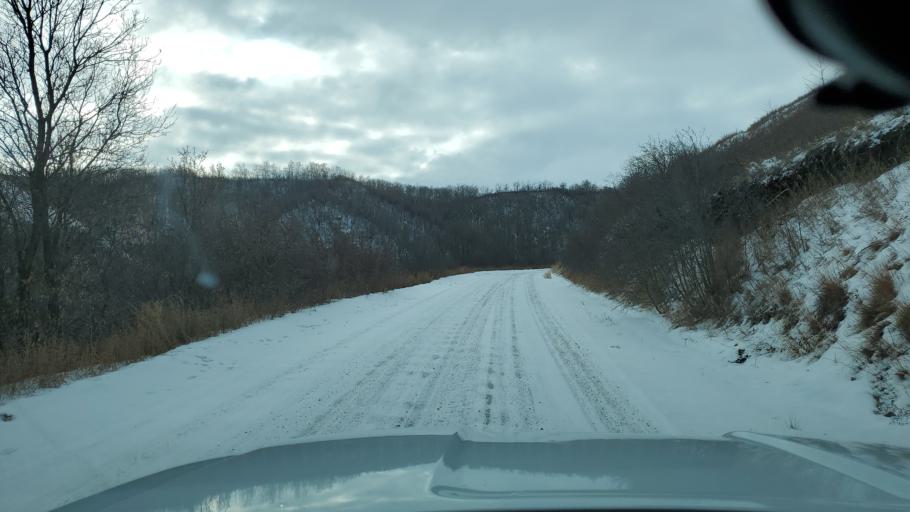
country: CA
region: Saskatchewan
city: White City
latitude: 50.7731
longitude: -104.1426
